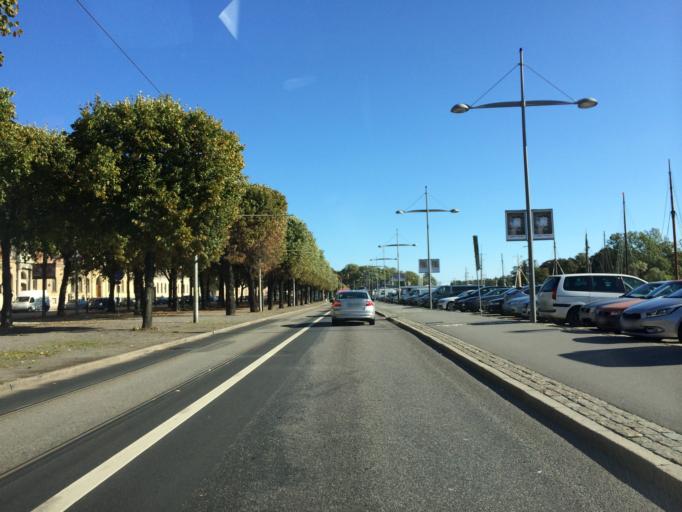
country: SE
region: Stockholm
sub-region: Stockholms Kommun
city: OEstermalm
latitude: 59.3316
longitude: 18.0877
